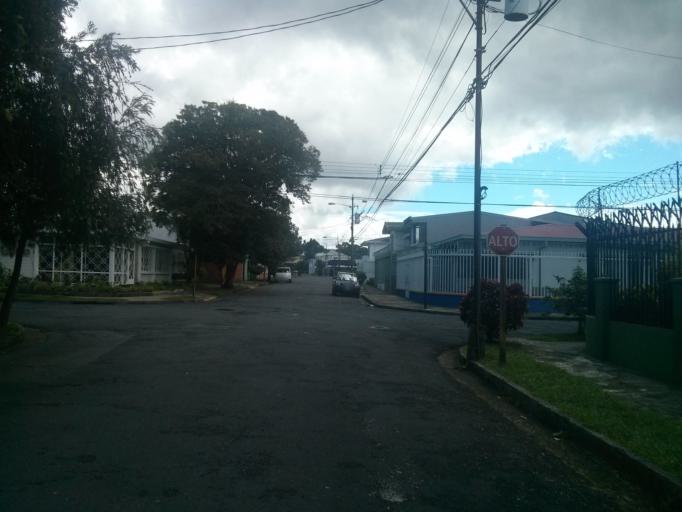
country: CR
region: San Jose
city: San Pedro
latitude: 9.9345
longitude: -84.0648
